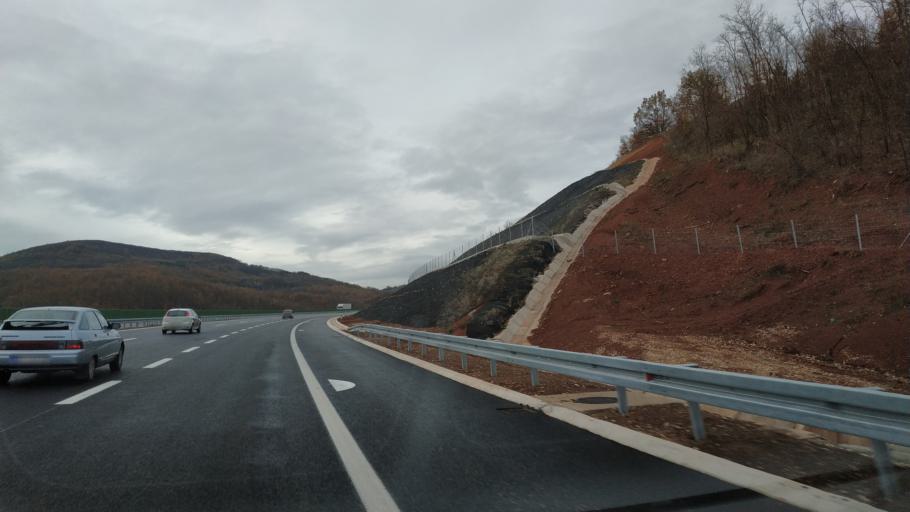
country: RS
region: Central Serbia
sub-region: Nisavski Okrug
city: Gadzin Han
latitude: 43.2580
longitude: 22.1499
